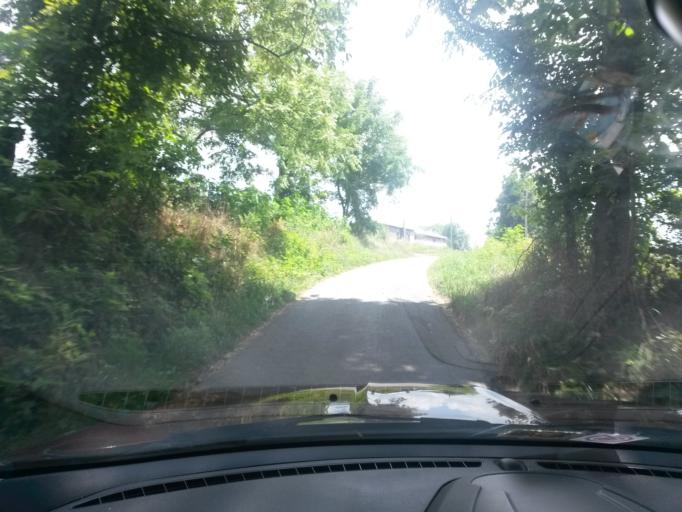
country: US
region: West Virginia
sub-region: Monroe County
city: Union
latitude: 37.5641
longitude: -80.5010
